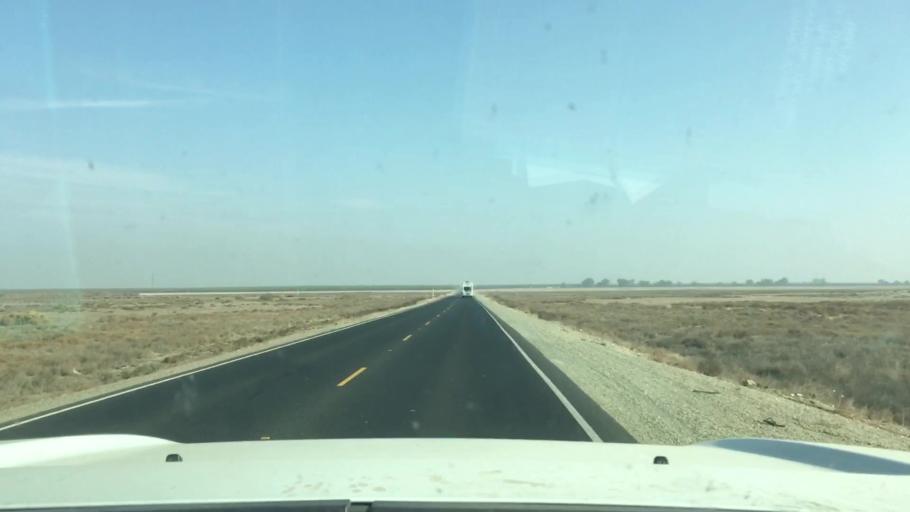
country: US
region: California
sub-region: Kern County
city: Lost Hills
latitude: 35.6159
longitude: -119.6064
